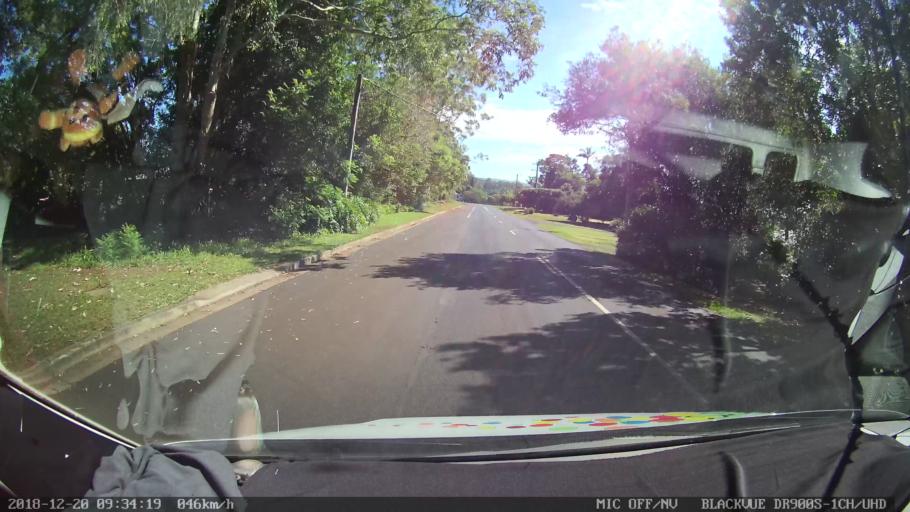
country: AU
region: New South Wales
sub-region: Lismore Municipality
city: Goonellabah
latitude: -28.6911
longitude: 153.3131
